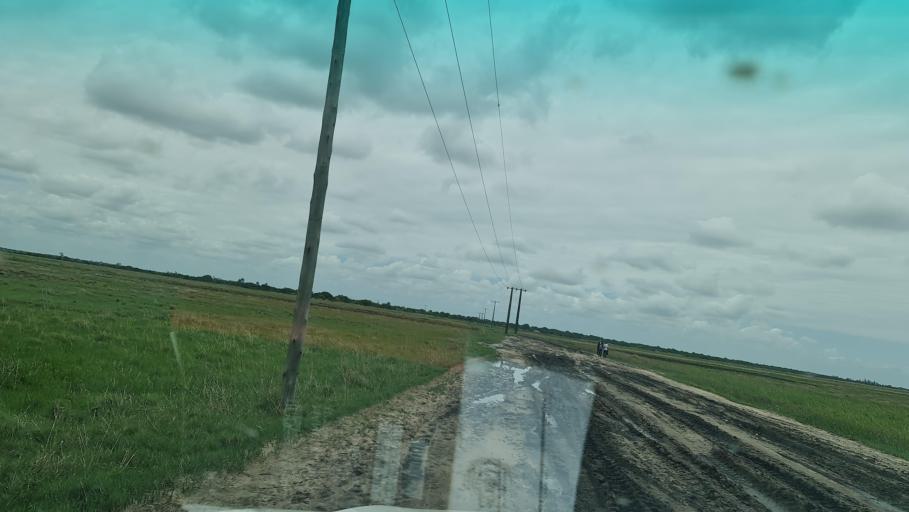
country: MZ
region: Maputo City
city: Maputo
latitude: -25.7116
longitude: 32.7029
